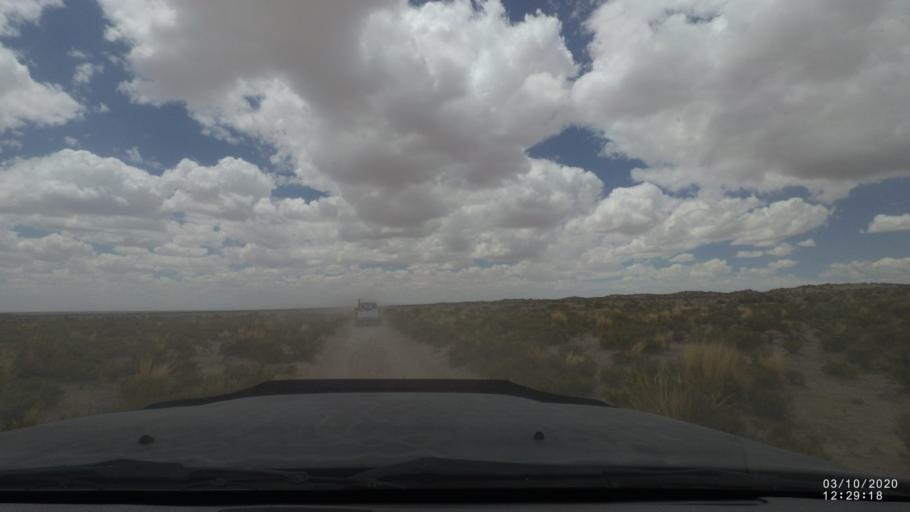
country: BO
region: Oruro
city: Poopo
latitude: -18.6894
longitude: -67.5484
